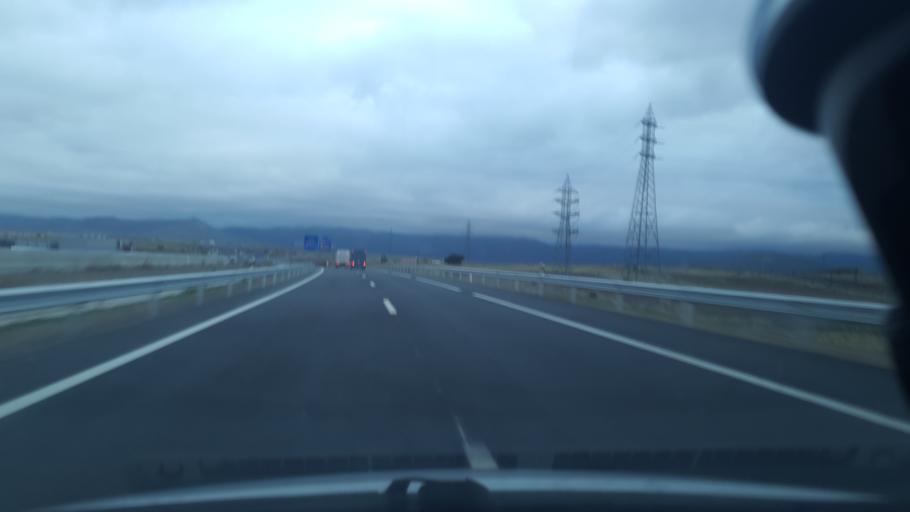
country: ES
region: Castille and Leon
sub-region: Provincia de Segovia
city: Segovia
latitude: 40.9184
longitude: -4.1215
